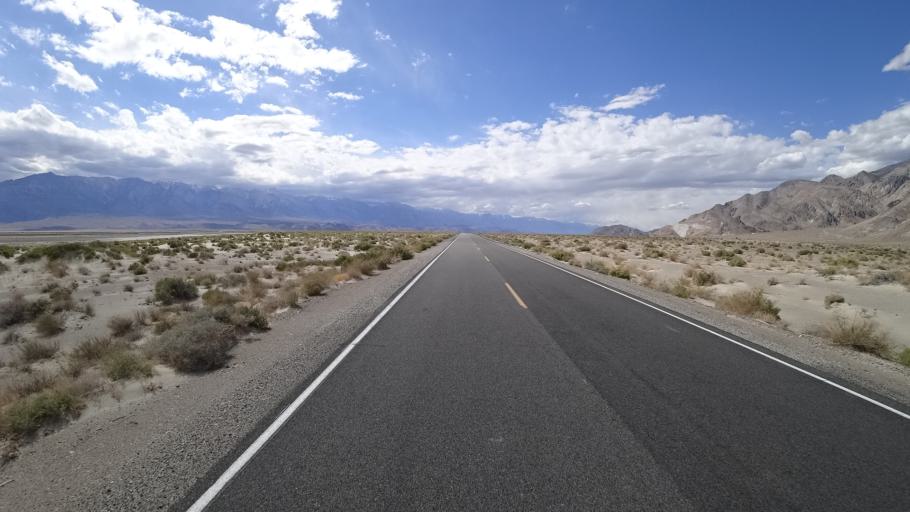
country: US
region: California
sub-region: Inyo County
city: Lone Pine
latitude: 36.5458
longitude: -117.9409
